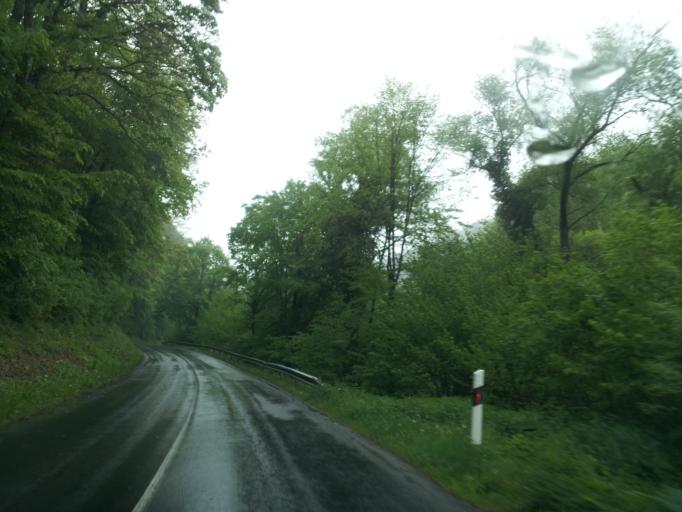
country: HU
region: Baranya
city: Komlo
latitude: 46.2162
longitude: 18.3010
